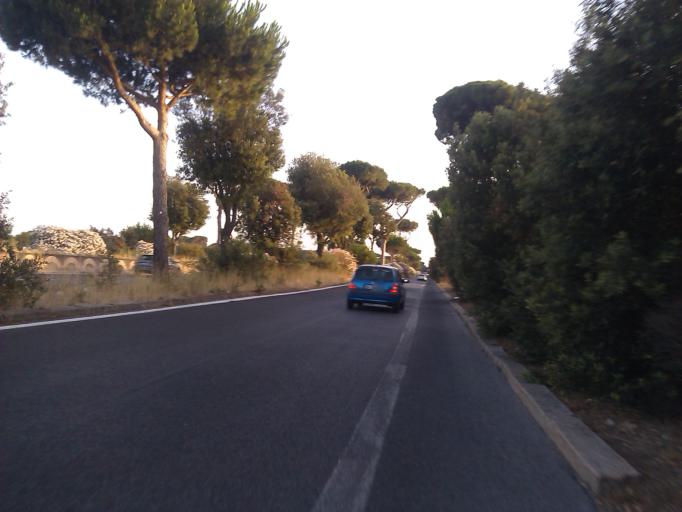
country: IT
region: Latium
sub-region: Citta metropolitana di Roma Capitale
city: Acilia-Castel Fusano-Ostia Antica
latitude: 41.7269
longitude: 12.3330
